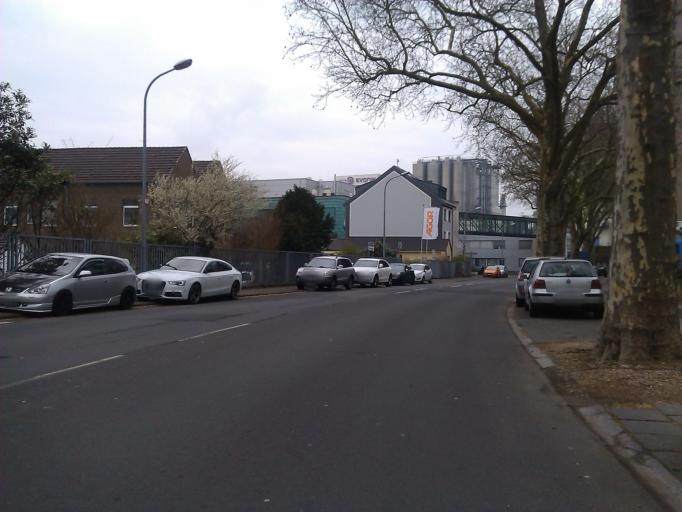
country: DE
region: North Rhine-Westphalia
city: Wesseling
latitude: 50.8302
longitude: 6.9756
